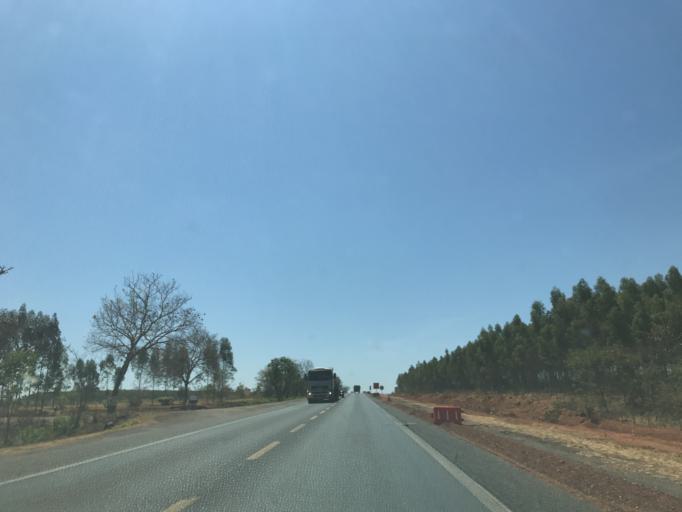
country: BR
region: Minas Gerais
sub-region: Prata
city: Prata
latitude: -19.4019
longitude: -48.8957
